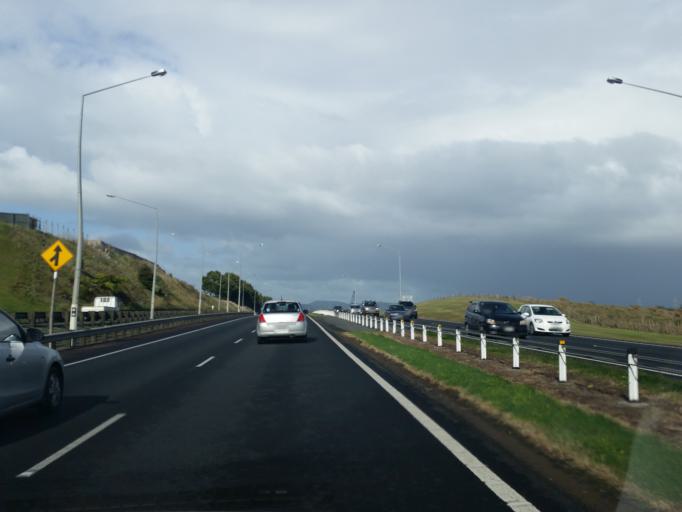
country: NZ
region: Auckland
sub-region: Auckland
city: Papakura
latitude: -37.0894
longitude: 174.9400
